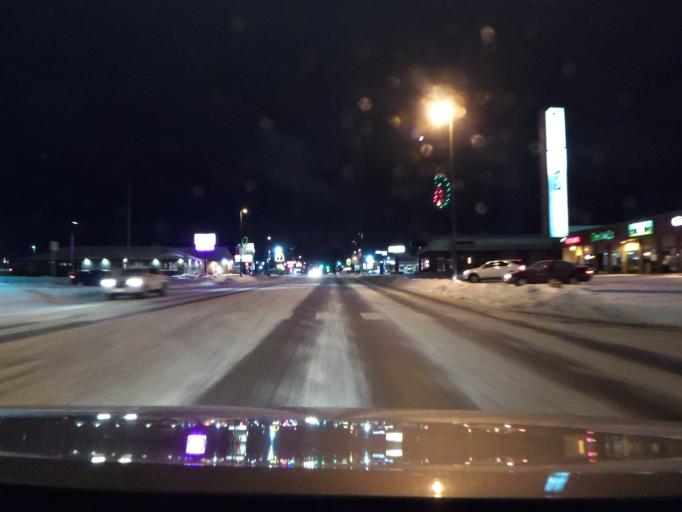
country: US
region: Wisconsin
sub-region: Dunn County
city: Menomonie
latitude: 44.8985
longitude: -91.9320
